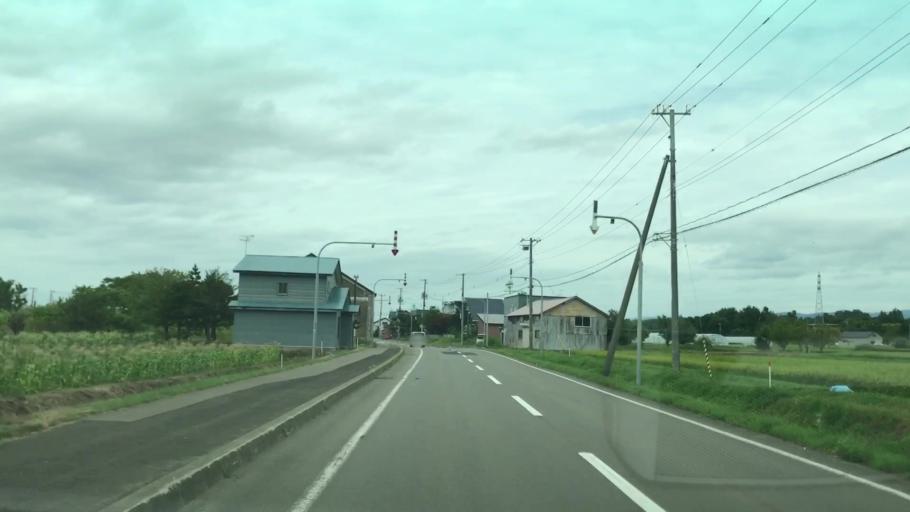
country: JP
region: Hokkaido
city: Iwanai
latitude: 42.9836
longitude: 140.6165
